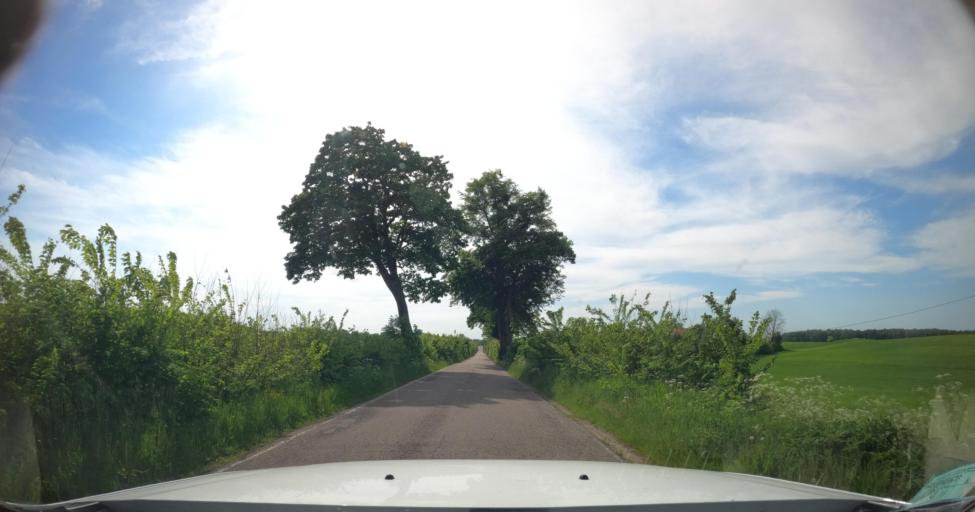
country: PL
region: Warmian-Masurian Voivodeship
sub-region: Powiat ostrodzki
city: Milakowo
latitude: 54.0096
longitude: 20.1308
